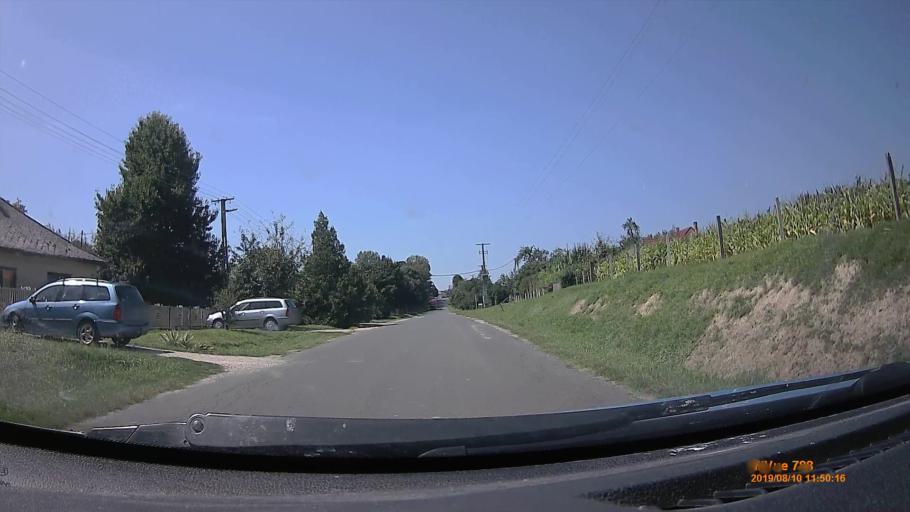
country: HU
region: Somogy
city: Somogyvar
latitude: 46.4934
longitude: 17.7206
